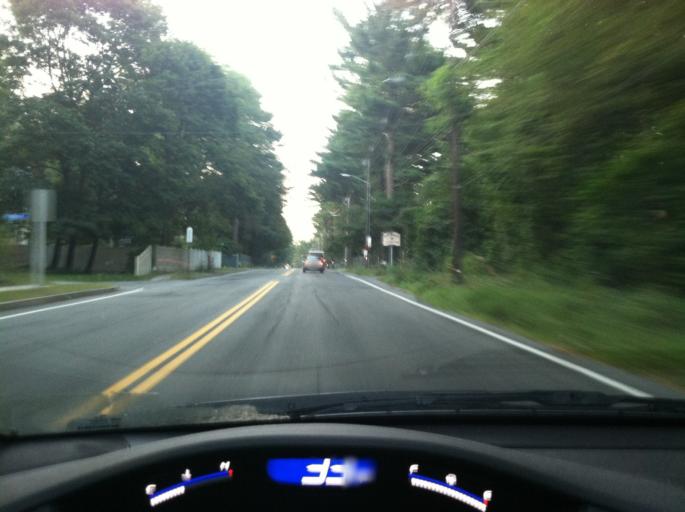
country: US
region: Massachusetts
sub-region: Middlesex County
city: Bedford
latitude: 42.4803
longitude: -71.2563
